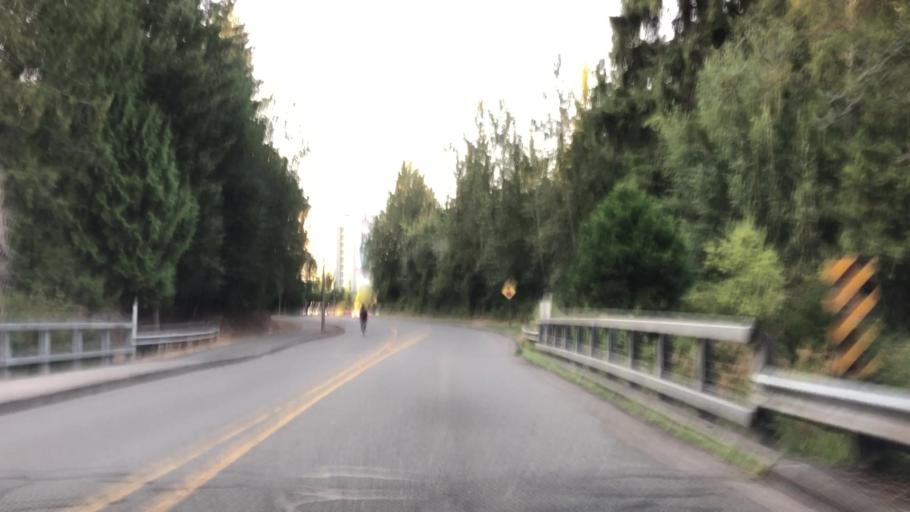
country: US
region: Washington
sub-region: Snohomish County
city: Marysville
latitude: 48.0834
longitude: -122.1891
